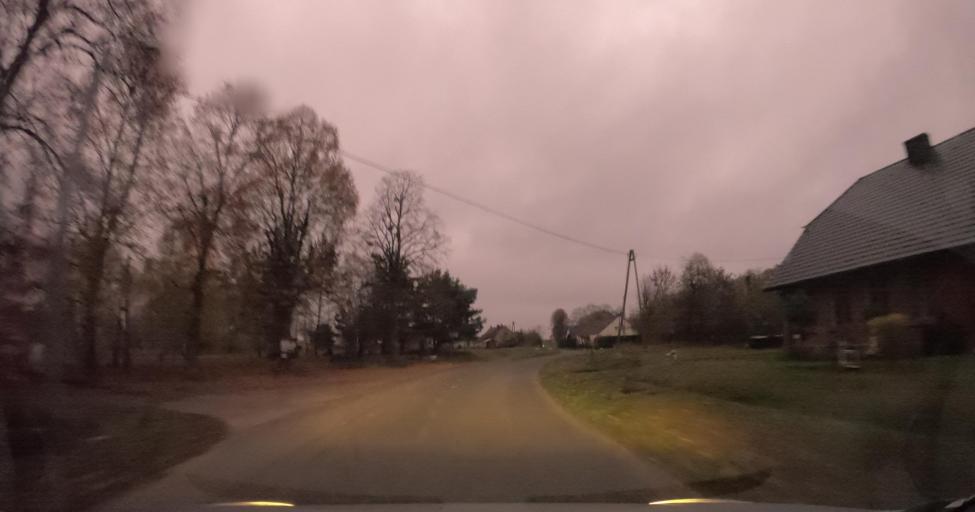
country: PL
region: West Pomeranian Voivodeship
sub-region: Powiat bialogardzki
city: Tychowo
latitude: 53.8751
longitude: 16.2344
